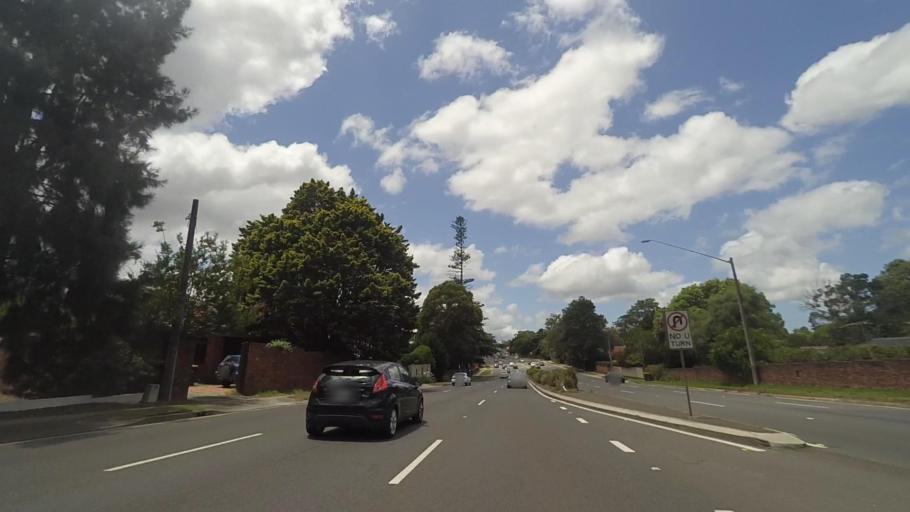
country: AU
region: New South Wales
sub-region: Ku-ring-gai
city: Normanhurst
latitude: -33.7239
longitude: 151.0989
